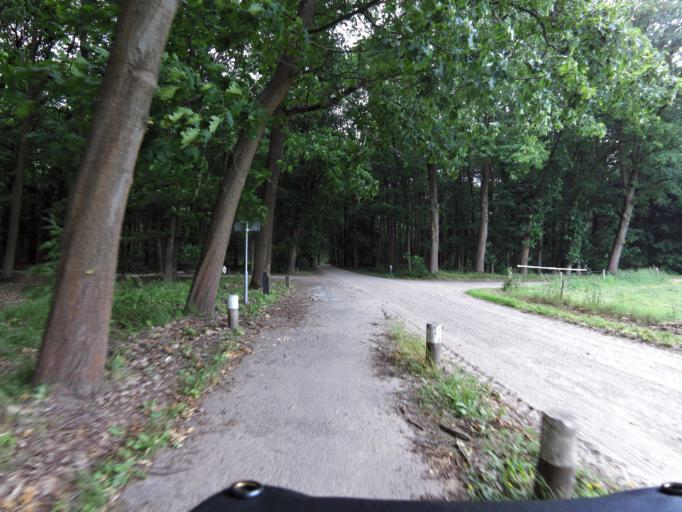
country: NL
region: North Brabant
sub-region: Gemeente Goirle
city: Goirle
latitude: 51.4781
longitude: 5.0764
